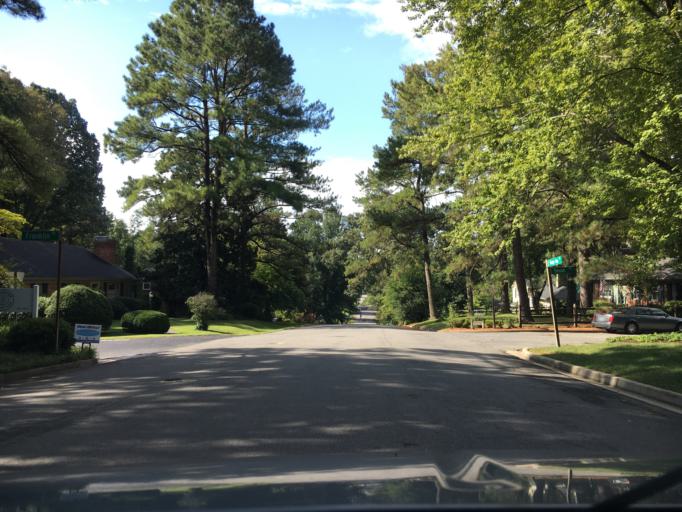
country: US
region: Virginia
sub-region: Henrico County
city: Tuckahoe
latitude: 37.5877
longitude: -77.5367
